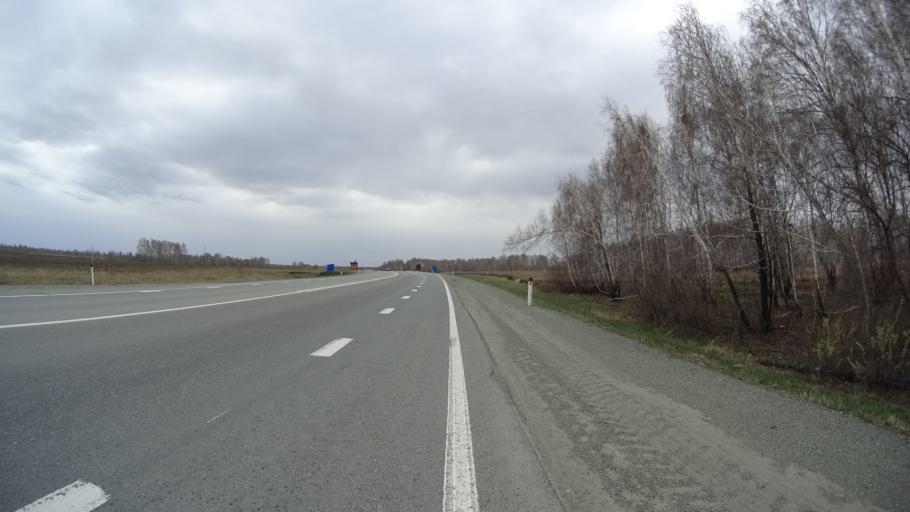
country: RU
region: Chelyabinsk
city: Yemanzhelinsk
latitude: 54.6977
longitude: 61.2504
